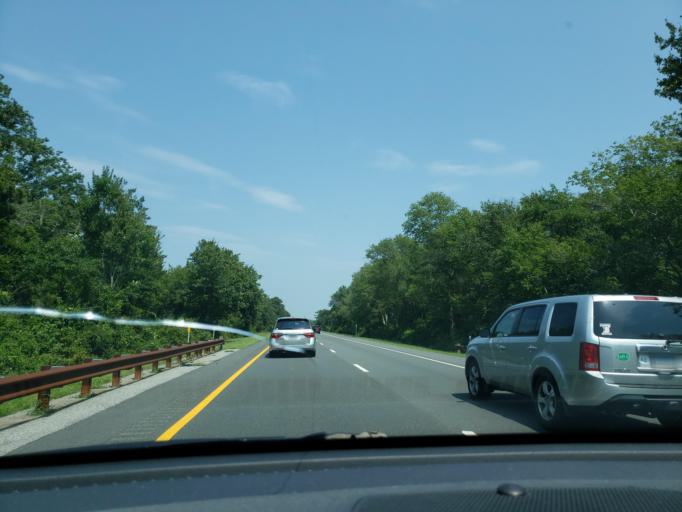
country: US
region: New Jersey
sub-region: Cape May County
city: Sea Isle City
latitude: 39.1641
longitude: -74.7374
